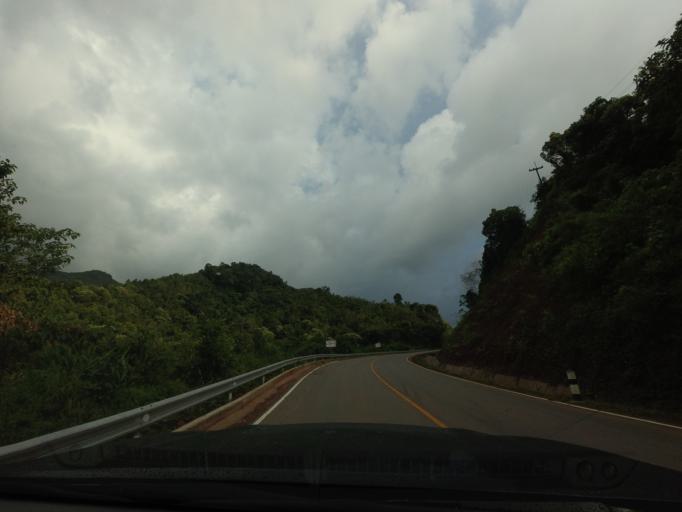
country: TH
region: Nan
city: Bo Kluea
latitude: 19.2651
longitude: 101.1784
